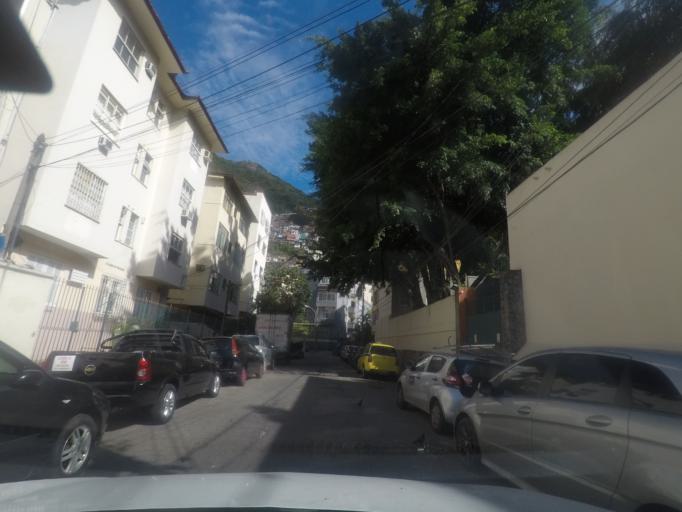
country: BR
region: Rio de Janeiro
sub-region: Rio De Janeiro
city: Rio de Janeiro
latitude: -22.9499
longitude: -43.1924
